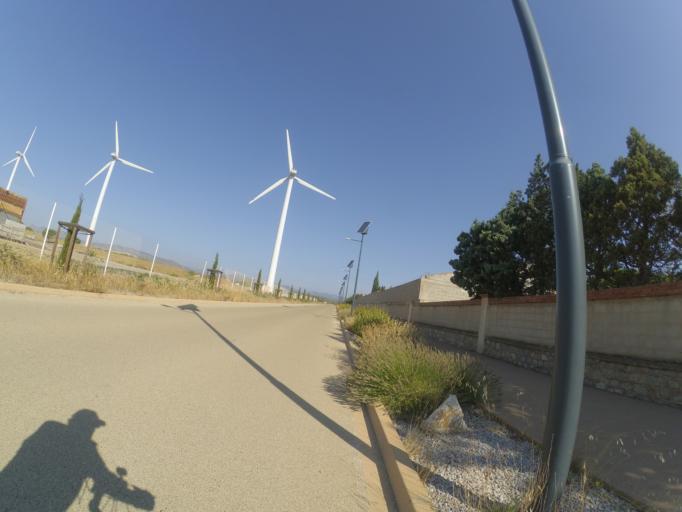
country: FR
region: Languedoc-Roussillon
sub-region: Departement des Pyrenees-Orientales
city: Salses-le-Chateau
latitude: 42.8044
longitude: 2.8928
